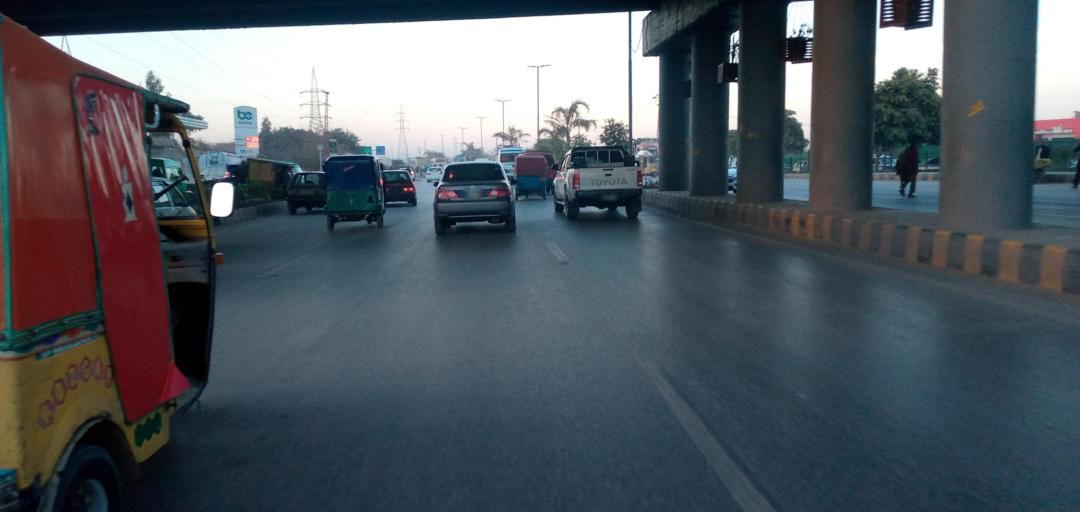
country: PK
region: Khyber Pakhtunkhwa
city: Peshawar
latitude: 34.0236
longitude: 71.6206
